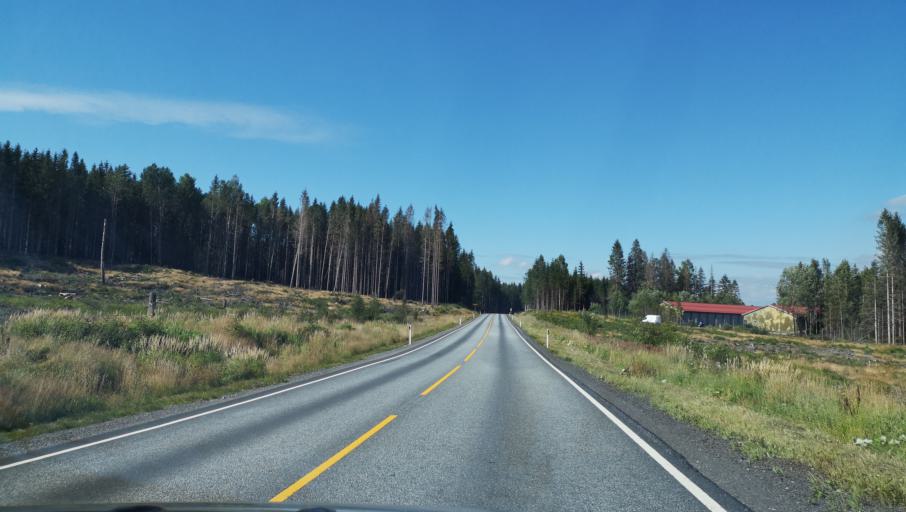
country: NO
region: Ostfold
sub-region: Valer
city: Kirkebygda
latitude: 59.5780
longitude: 10.8754
